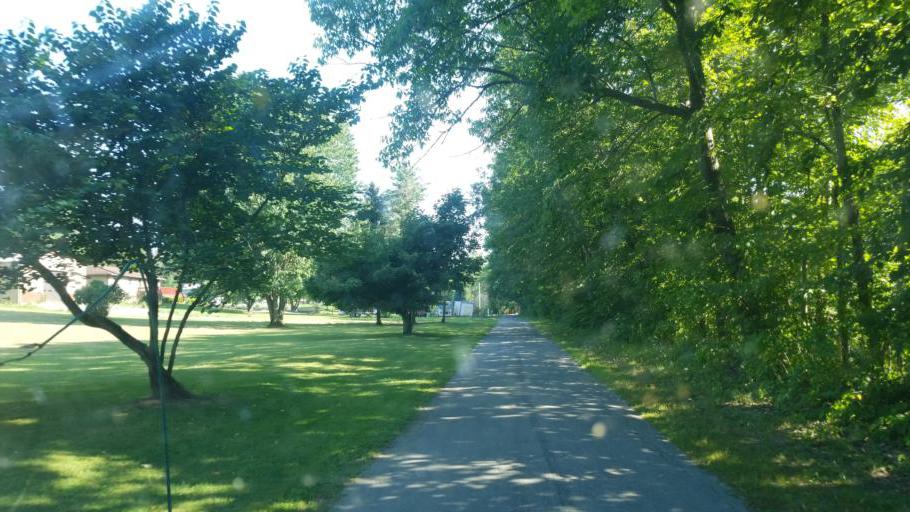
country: US
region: Ohio
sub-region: Wyandot County
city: Upper Sandusky
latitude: 40.7769
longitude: -83.2269
